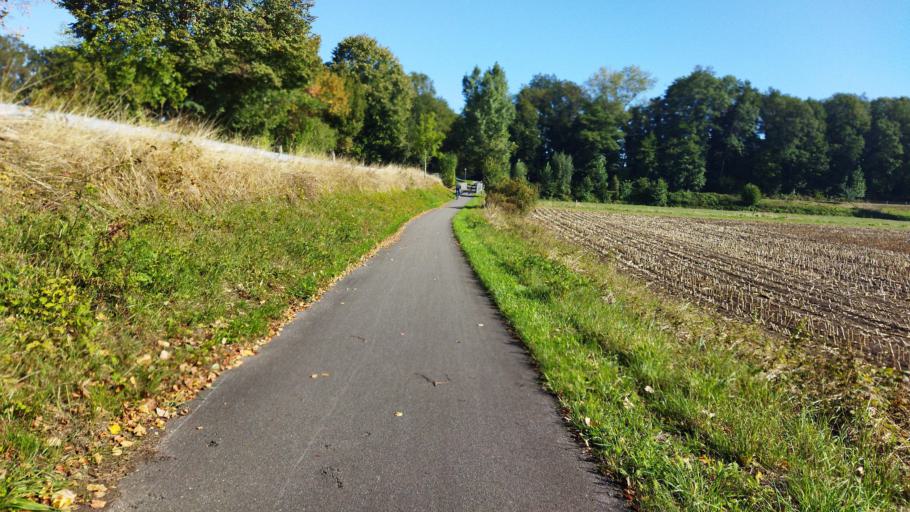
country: DE
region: North Rhine-Westphalia
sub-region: Regierungsbezirk Munster
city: Wettringen
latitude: 52.2446
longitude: 7.3128
